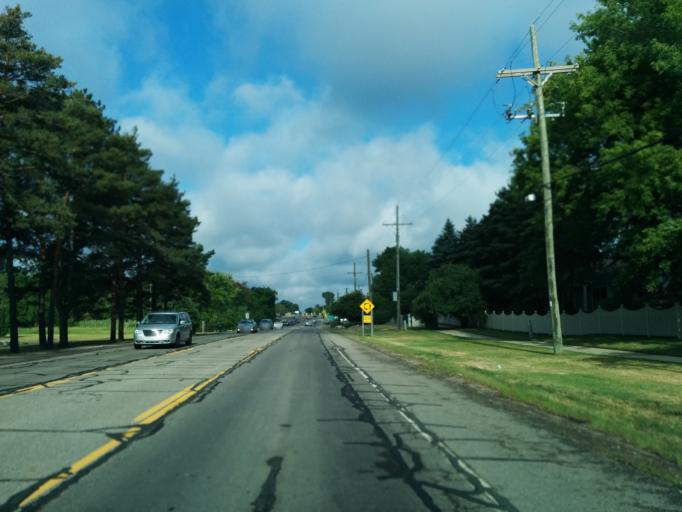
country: US
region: Michigan
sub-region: Oakland County
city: West Bloomfield Township
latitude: 42.5280
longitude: -83.3739
